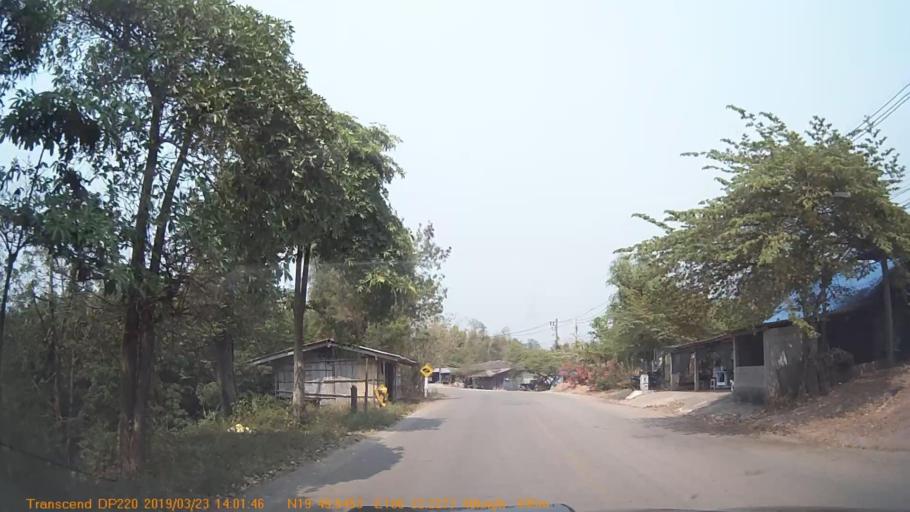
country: TH
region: Chiang Rai
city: Khun Tan
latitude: 19.8279
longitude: 100.3707
